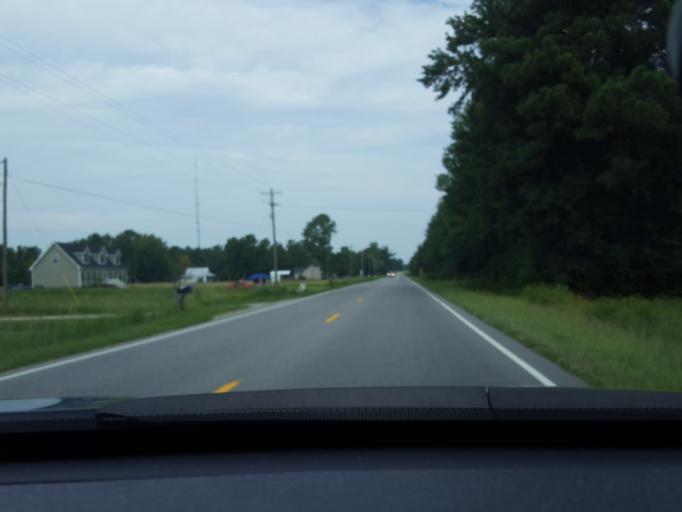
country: US
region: North Carolina
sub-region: Chowan County
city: Edenton
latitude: 36.1253
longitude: -76.6507
